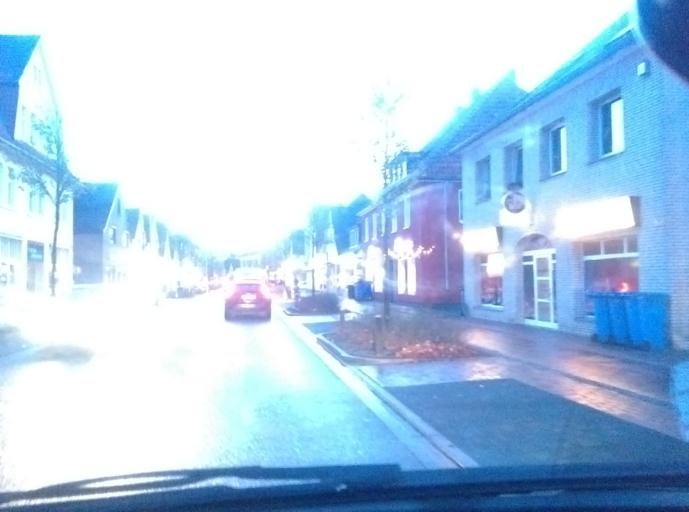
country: DE
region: Lower Saxony
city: Oldenburg
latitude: 53.1331
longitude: 8.1950
